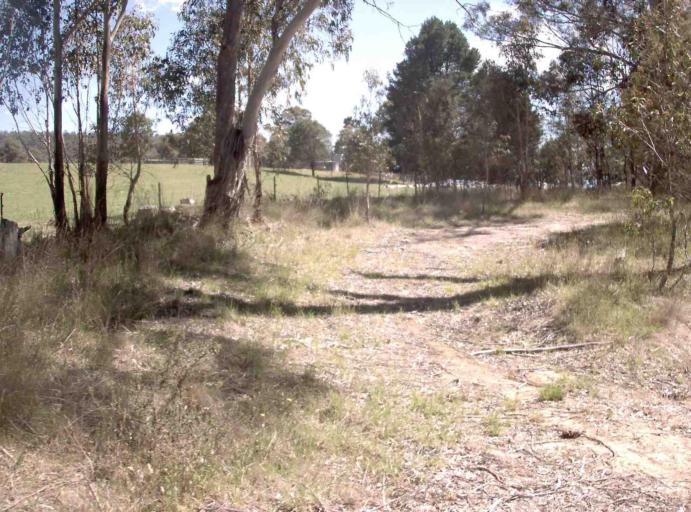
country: AU
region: New South Wales
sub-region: Bombala
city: Bombala
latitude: -37.0575
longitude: 148.8033
